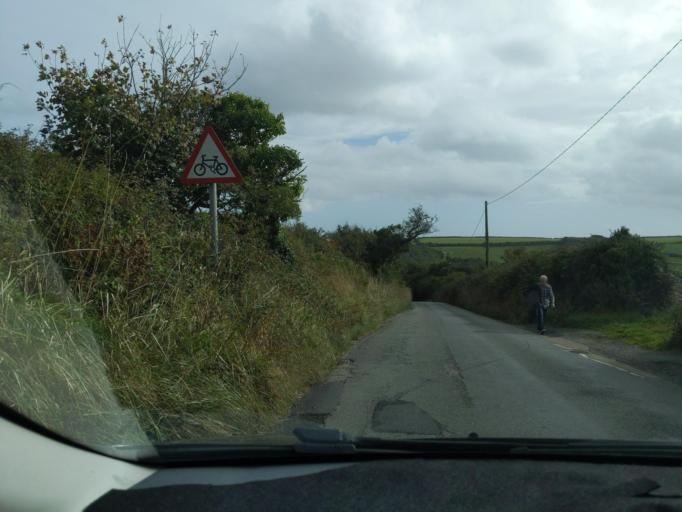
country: GB
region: England
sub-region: Cornwall
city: Mevagissey
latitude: 50.2438
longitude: -4.8003
